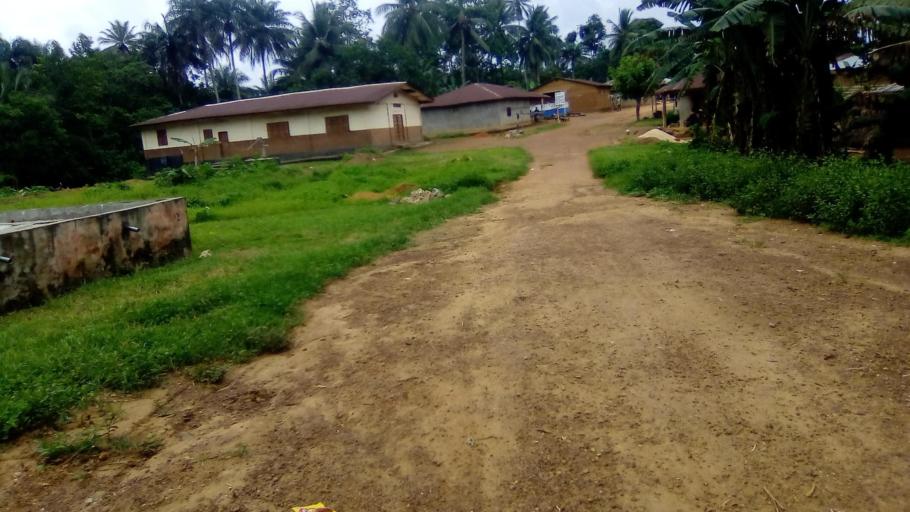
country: SL
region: Southern Province
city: Pujehun
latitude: 7.3722
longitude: -11.7103
